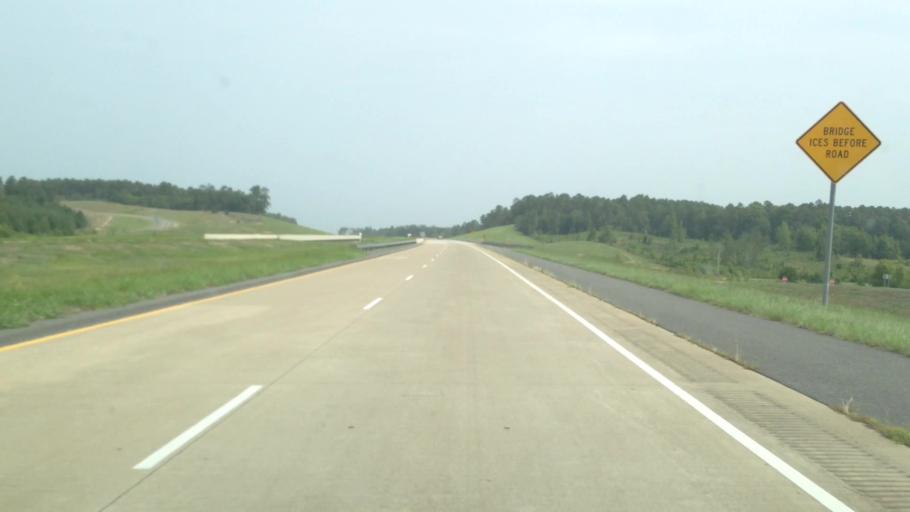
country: US
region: Louisiana
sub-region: Caddo Parish
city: Vivian
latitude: 32.9409
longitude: -93.8972
